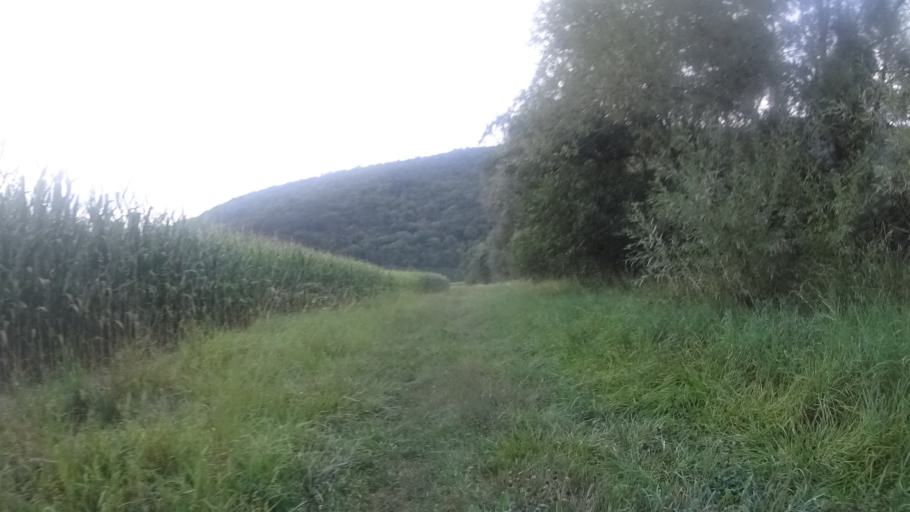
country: FR
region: Franche-Comte
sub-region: Departement du Doubs
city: Thise
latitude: 47.2609
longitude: 6.0788
